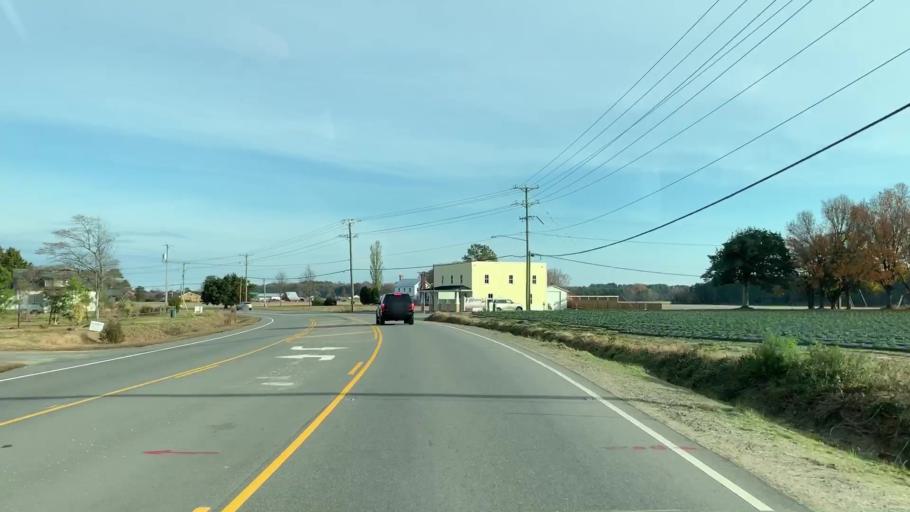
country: US
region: Virginia
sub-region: City of Virginia Beach
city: Virginia Beach
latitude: 36.6935
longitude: -76.0245
